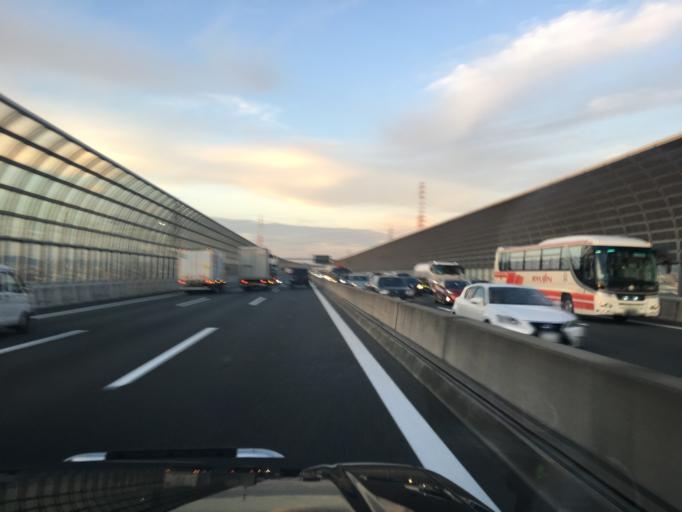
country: JP
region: Osaka
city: Daitocho
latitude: 34.7327
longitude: 135.6077
